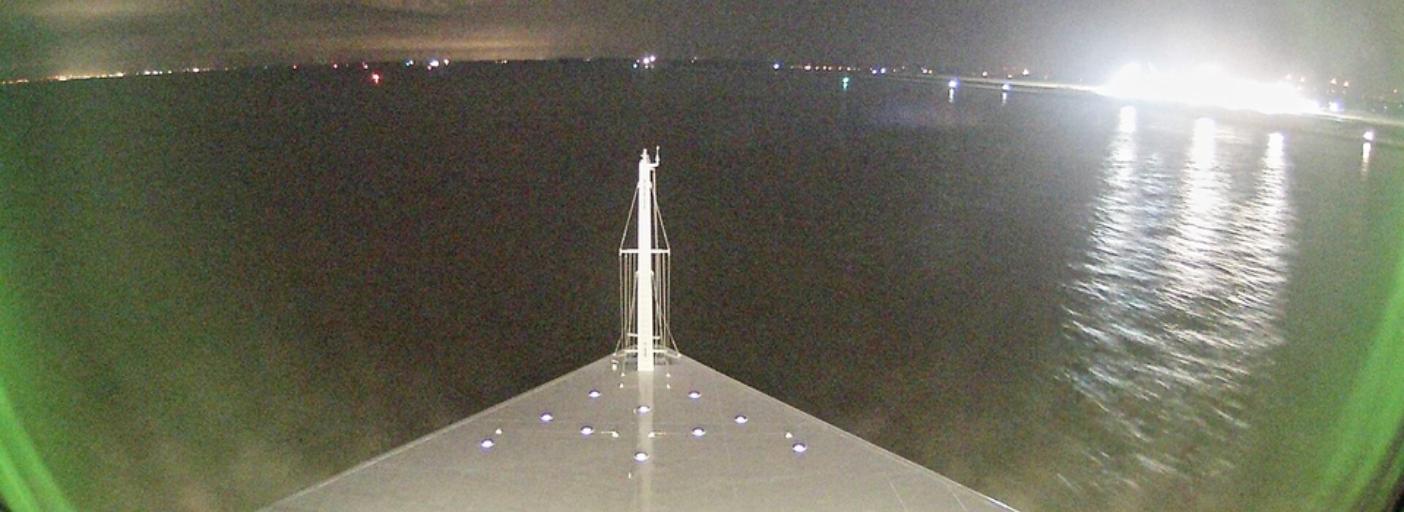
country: DE
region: Lower Saxony
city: Nordleda
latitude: 53.8391
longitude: 8.7934
